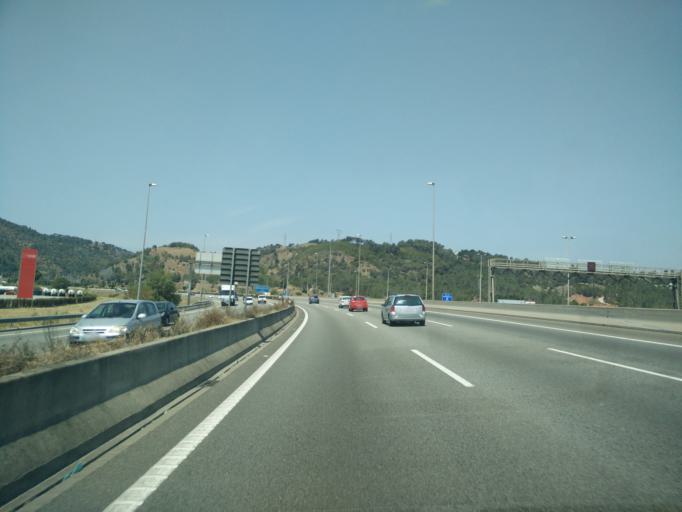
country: ES
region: Catalonia
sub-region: Provincia de Barcelona
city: Castellbisbal
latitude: 41.4713
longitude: 1.9606
